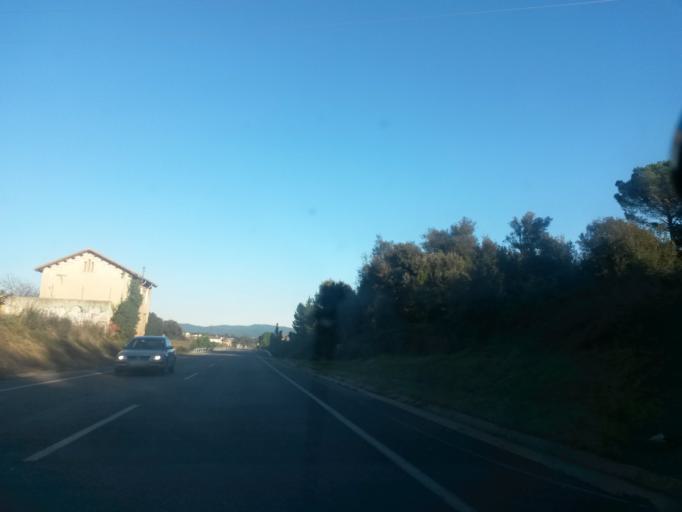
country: ES
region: Catalonia
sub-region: Provincia de Girona
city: Aiguaviva
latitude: 41.9346
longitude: 2.7534
